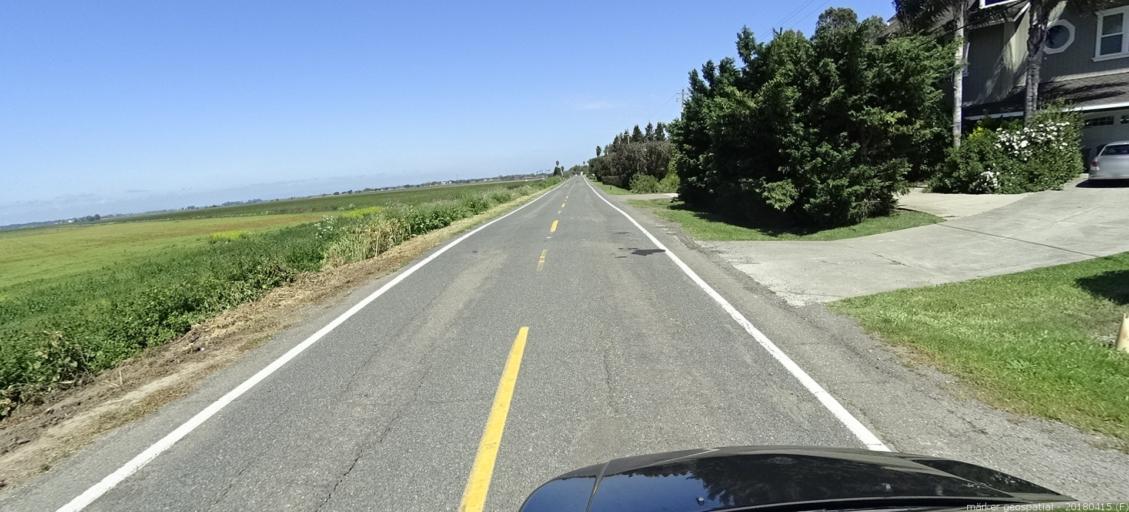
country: US
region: California
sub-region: Solano County
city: Rio Vista
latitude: 38.1372
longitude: -121.5970
